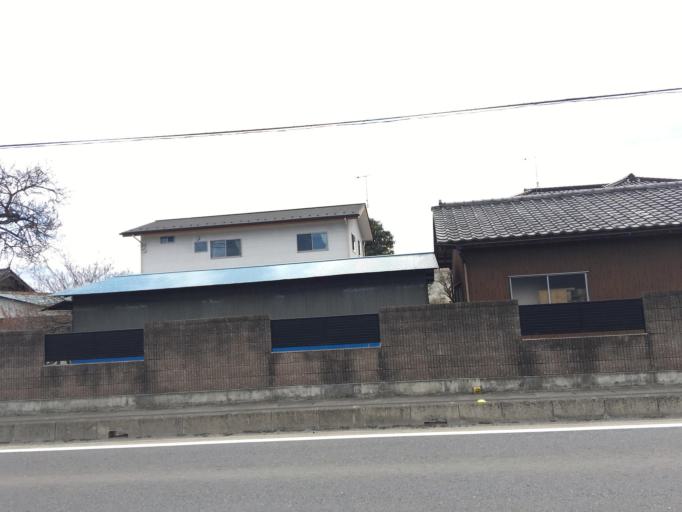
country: JP
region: Saitama
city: Yorii
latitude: 36.1119
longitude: 139.2436
